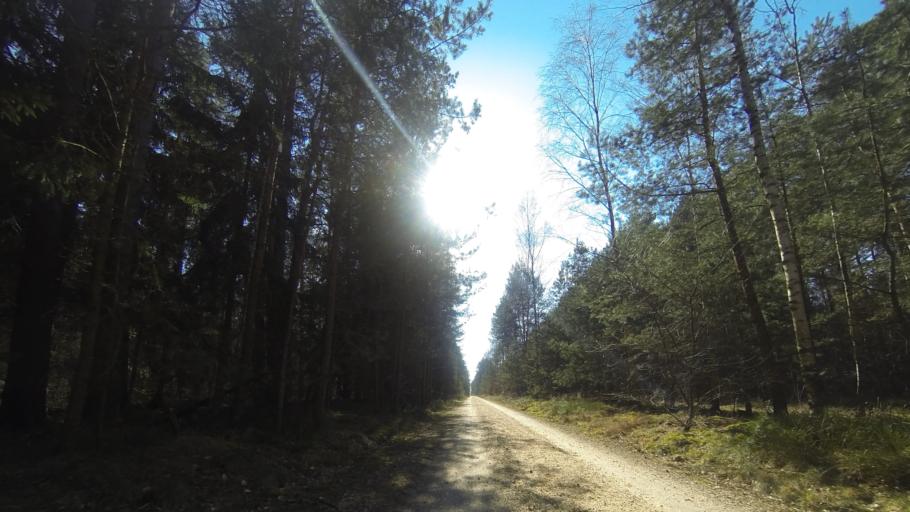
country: DE
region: Saxony
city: Laussnitz
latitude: 51.2531
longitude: 13.8455
